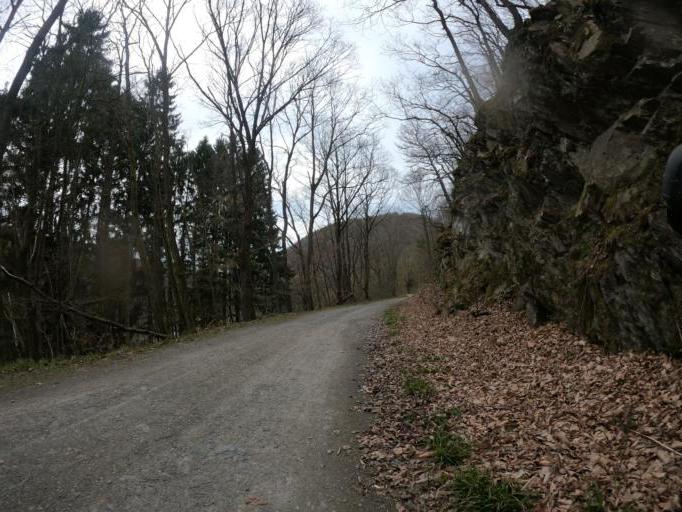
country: DE
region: North Rhine-Westphalia
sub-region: Regierungsbezirk Koln
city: Hurtgenwald
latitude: 50.6822
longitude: 6.4177
